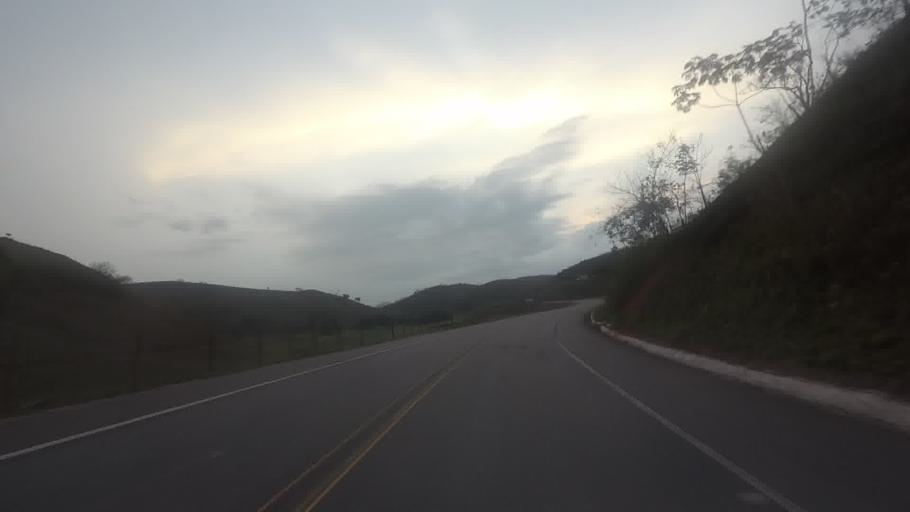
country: BR
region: Rio de Janeiro
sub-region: Carmo
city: Carmo
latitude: -21.8412
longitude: -42.6224
